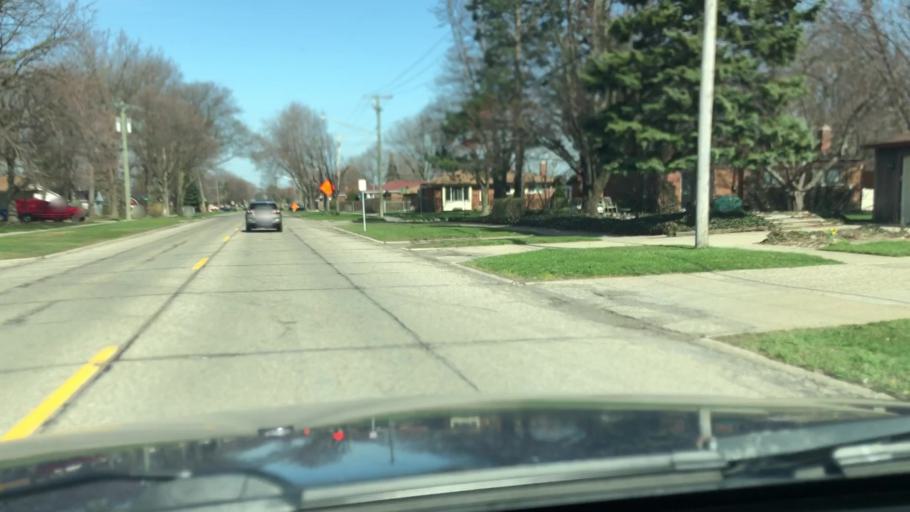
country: US
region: Michigan
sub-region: Macomb County
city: Center Line
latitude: 42.5000
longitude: -83.0007
